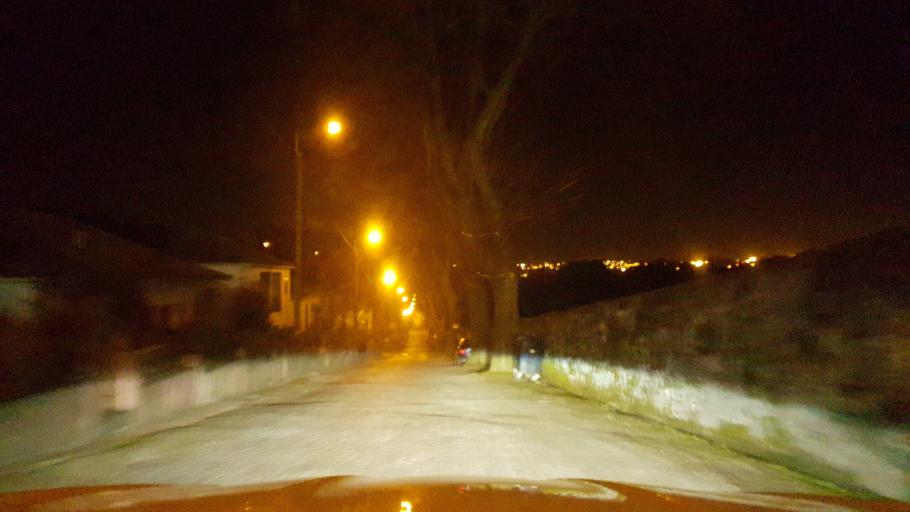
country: PT
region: Porto
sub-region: Matosinhos
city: Santa Cruz do Bispo
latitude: 41.2206
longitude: -8.6693
